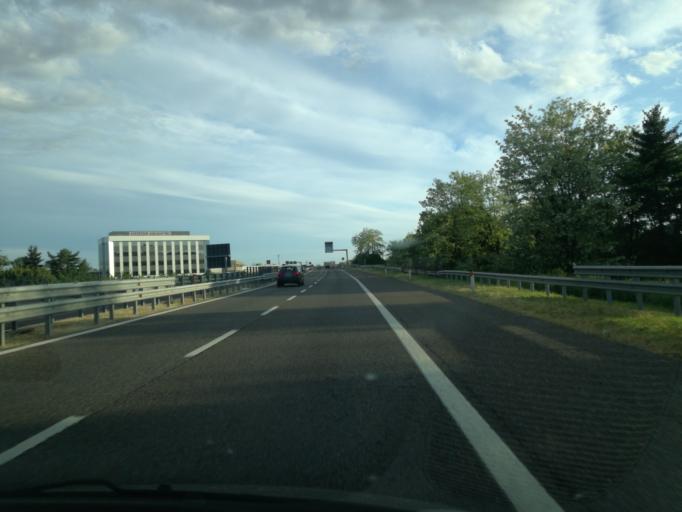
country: IT
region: Lombardy
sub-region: Provincia di Monza e Brianza
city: Agrate Brianza
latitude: 45.5698
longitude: 9.3379
